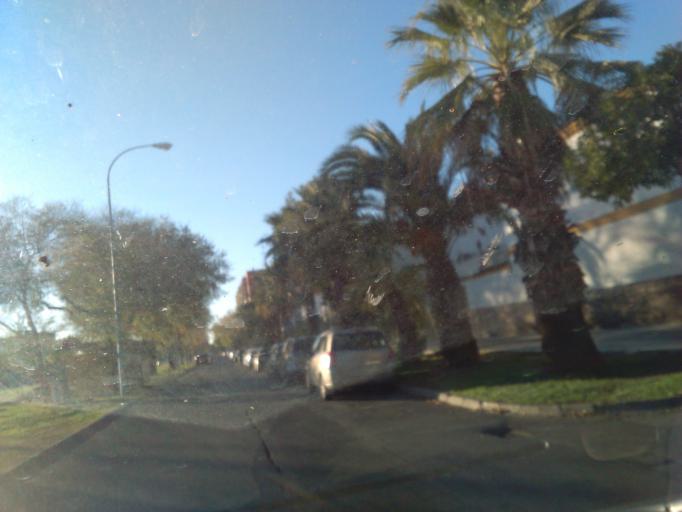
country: ES
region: Andalusia
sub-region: Provincia de Sevilla
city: Sevilla
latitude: 37.3907
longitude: -5.9165
